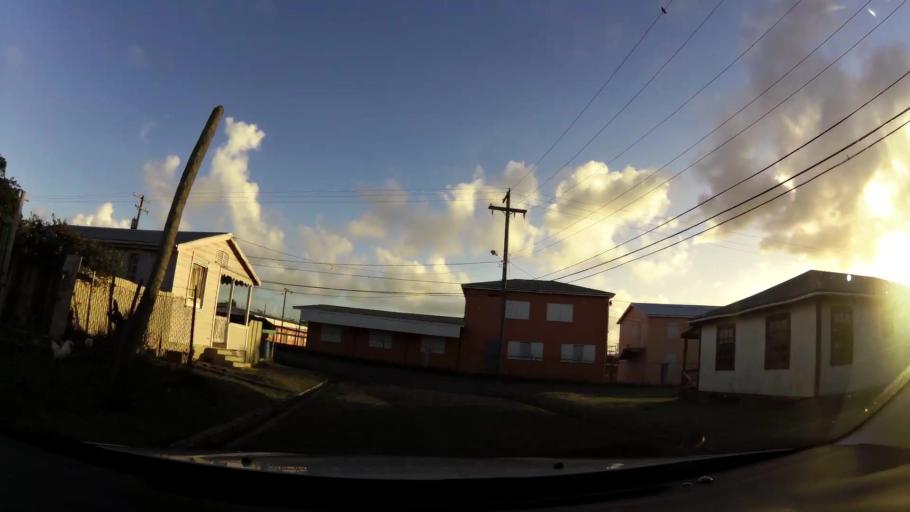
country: AG
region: Saint John
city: Saint John's
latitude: 17.1294
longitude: -61.8487
